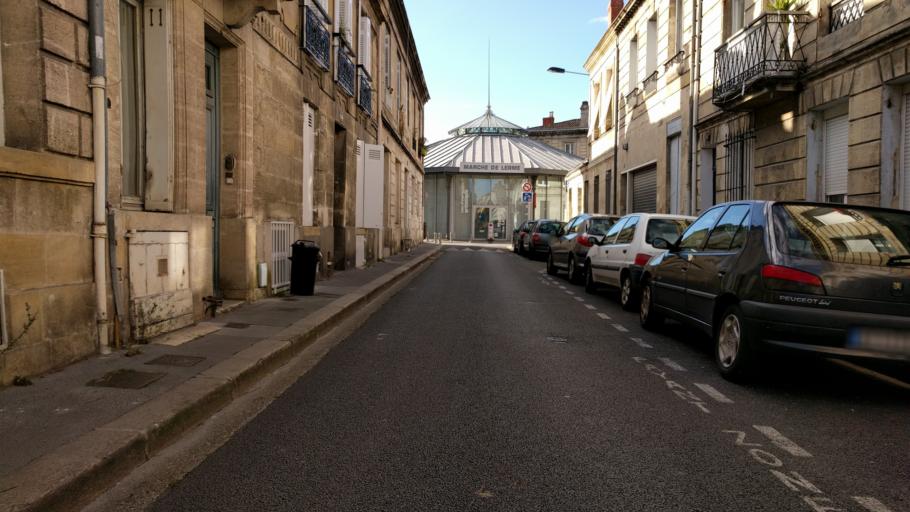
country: FR
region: Aquitaine
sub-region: Departement de la Gironde
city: Bordeaux
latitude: 44.8473
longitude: -0.5849
